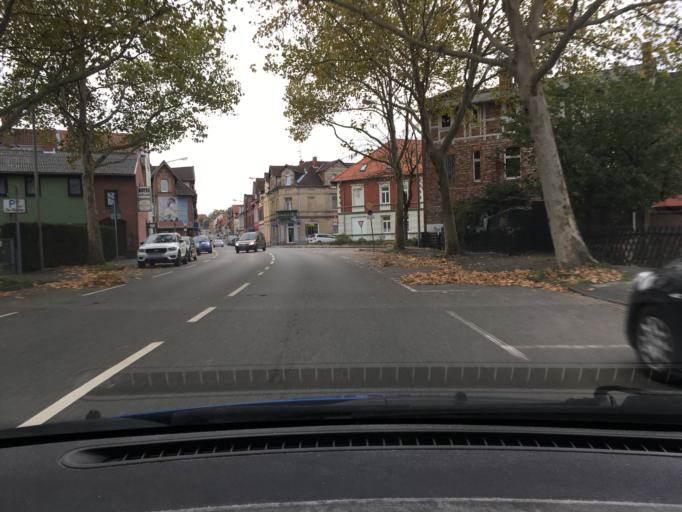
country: DE
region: Lower Saxony
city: Helmstedt
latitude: 52.2319
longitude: 11.0054
